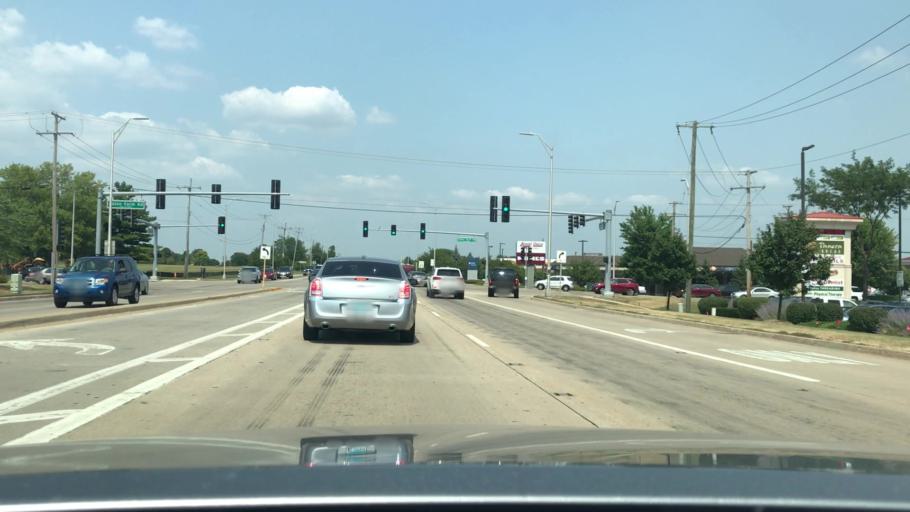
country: US
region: Illinois
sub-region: Will County
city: Crystal Lawns
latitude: 41.5645
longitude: -88.2003
